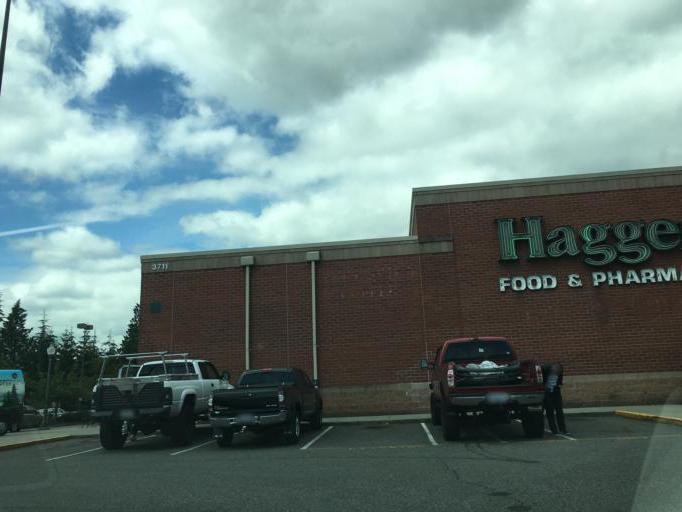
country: US
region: Washington
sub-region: Snohomish County
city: Marysville
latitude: 48.0764
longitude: -122.1809
